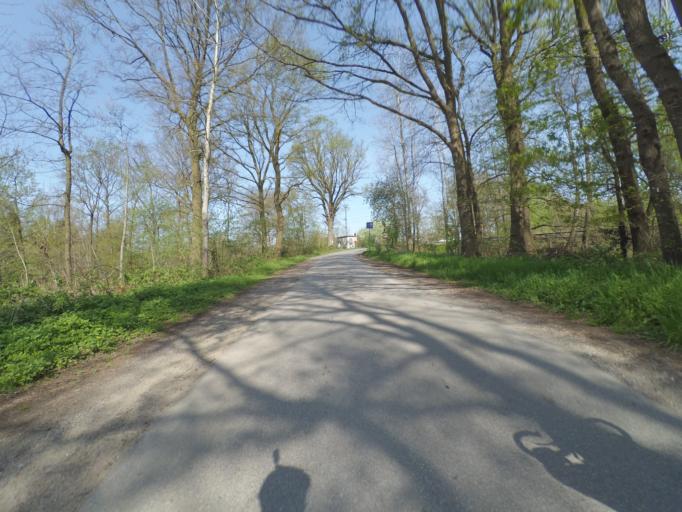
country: DE
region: North Rhine-Westphalia
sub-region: Regierungsbezirk Dusseldorf
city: Mehrhoog
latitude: 51.7328
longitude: 6.5299
